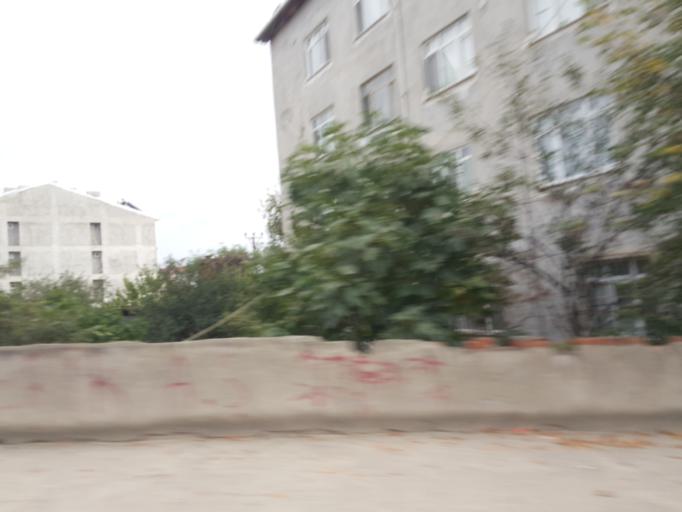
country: TR
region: Sinop
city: Duragan
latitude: 41.4200
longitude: 35.0537
